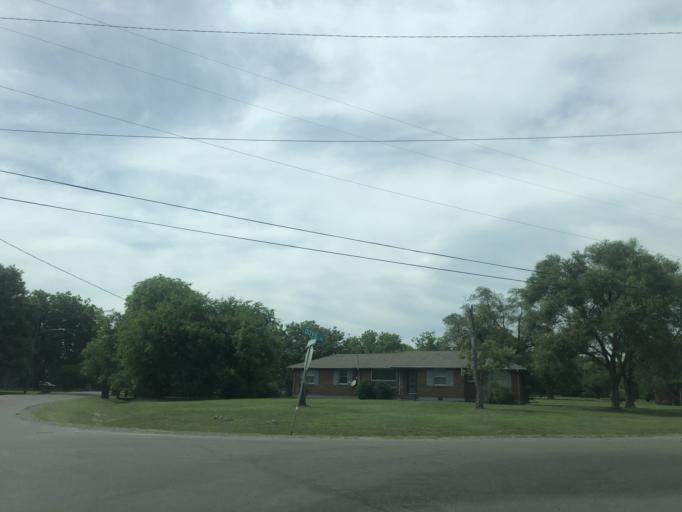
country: US
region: Tennessee
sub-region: Davidson County
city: Nashville
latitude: 36.2119
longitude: -86.8316
